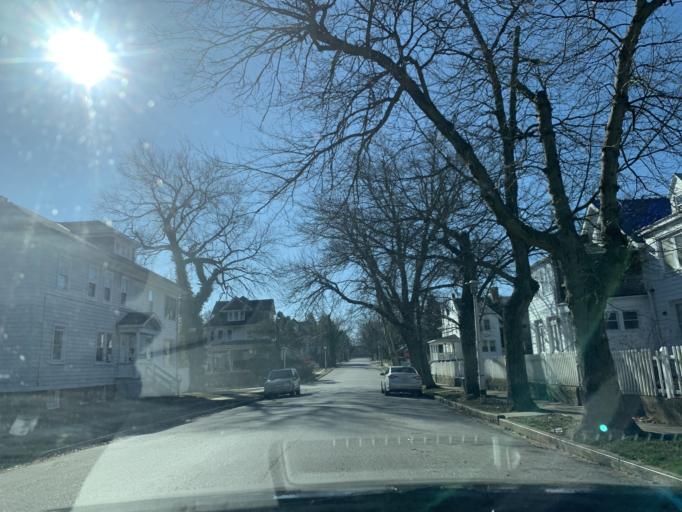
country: US
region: Maryland
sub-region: Baltimore County
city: Lochearn
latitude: 39.3243
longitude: -76.6772
